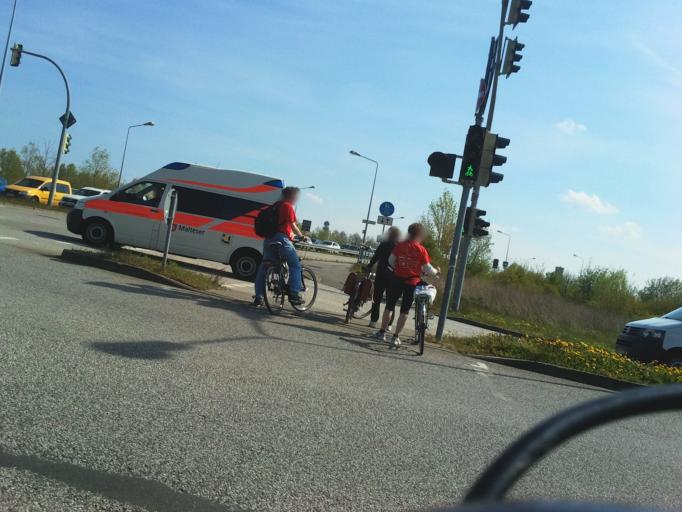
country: DE
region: Mecklenburg-Vorpommern
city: Warnemuende
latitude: 54.1383
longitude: 12.0789
